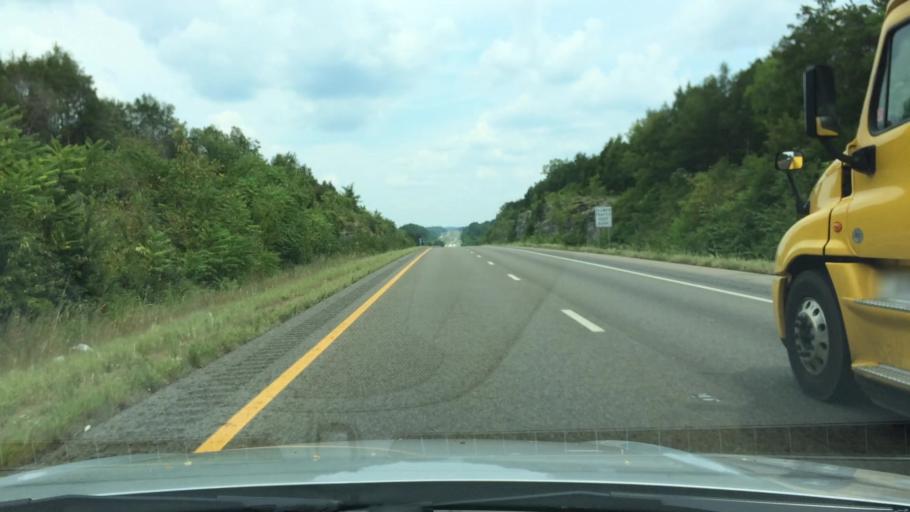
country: US
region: Tennessee
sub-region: Maury County
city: Columbia
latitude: 35.5586
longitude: -86.9068
